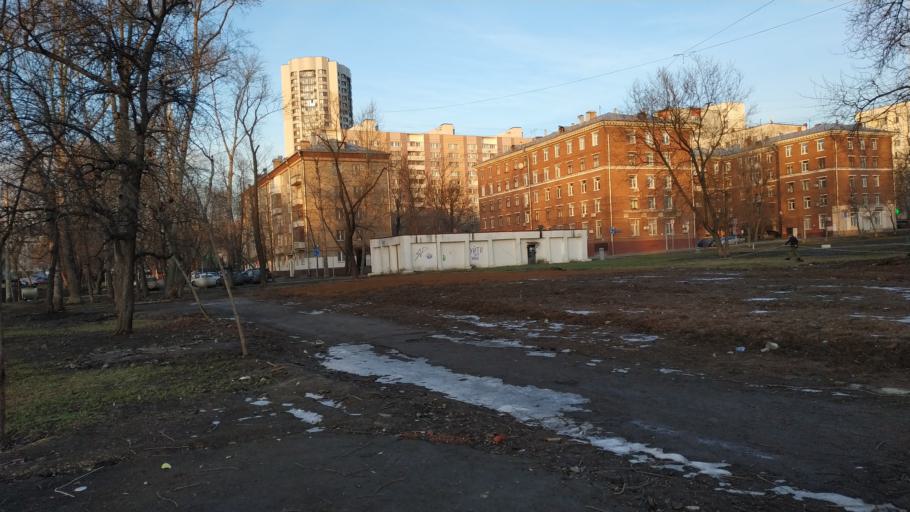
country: RU
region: Moscow
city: Mar'ina Roshcha
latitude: 55.8051
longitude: 37.6105
